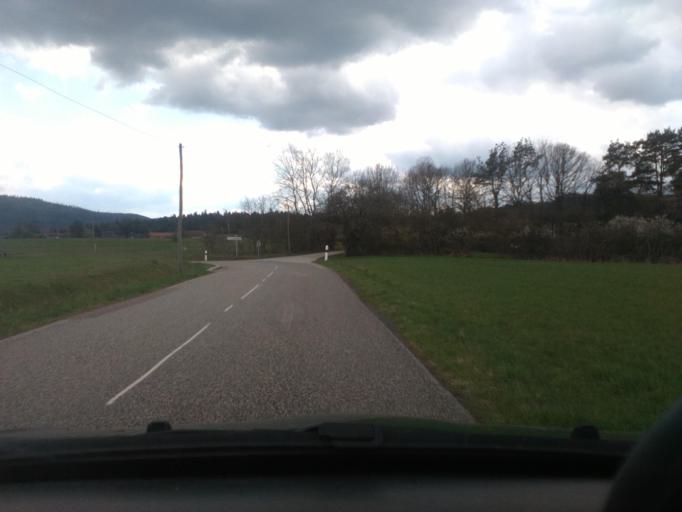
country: FR
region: Lorraine
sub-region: Departement des Vosges
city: Etival-Clairefontaine
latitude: 48.3294
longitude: 6.8261
